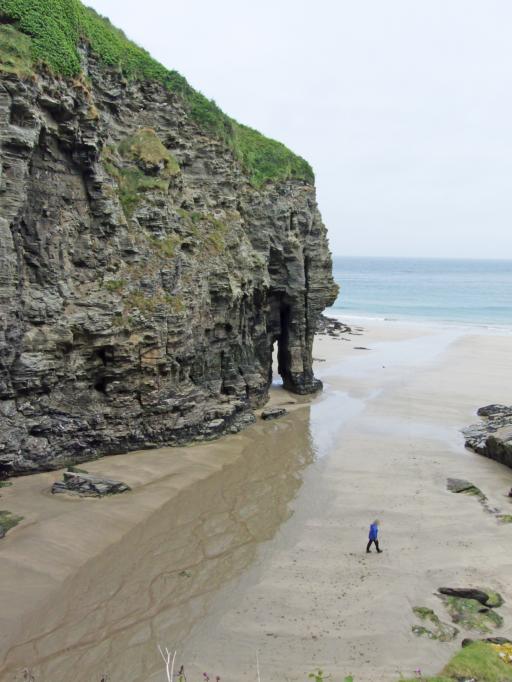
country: GB
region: England
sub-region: Cornwall
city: Tintagel
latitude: 50.6715
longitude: -4.7376
